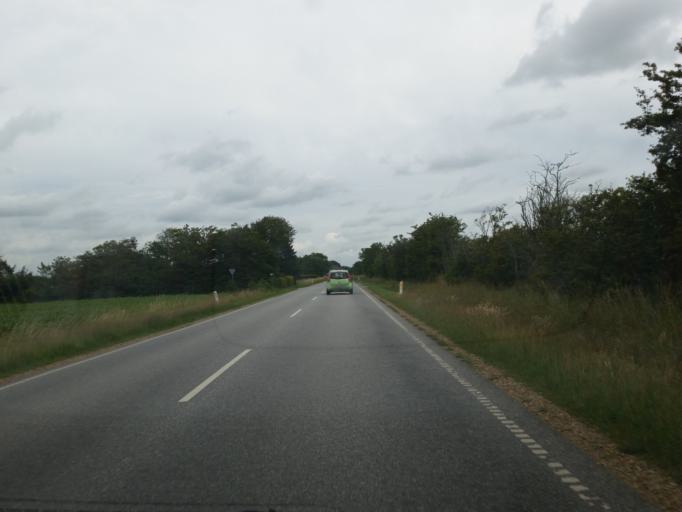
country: DK
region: South Denmark
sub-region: Esbjerg Kommune
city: Ribe
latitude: 55.3853
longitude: 8.8547
